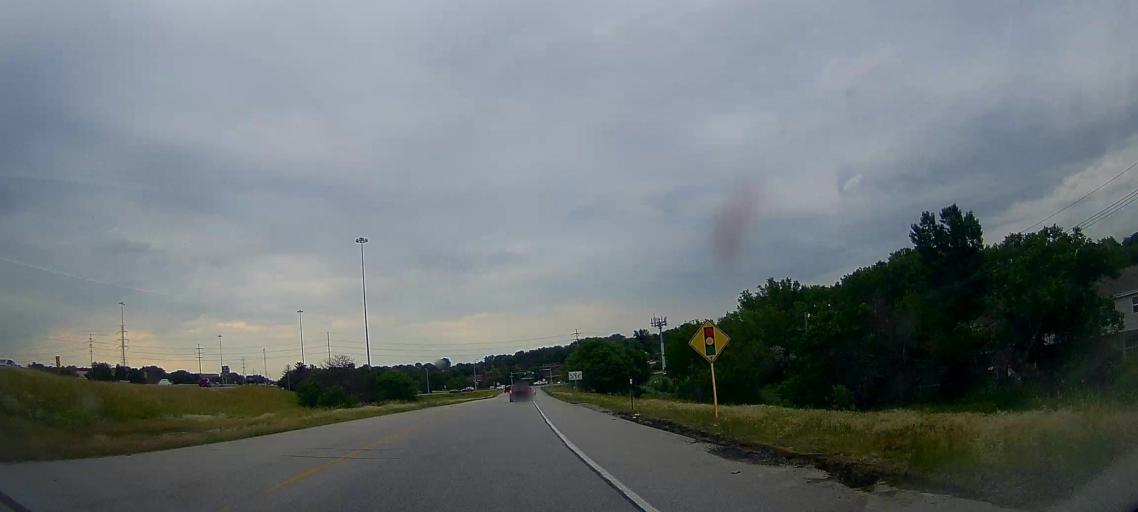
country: US
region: Nebraska
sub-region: Douglas County
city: Ralston
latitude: 41.3047
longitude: -96.0702
